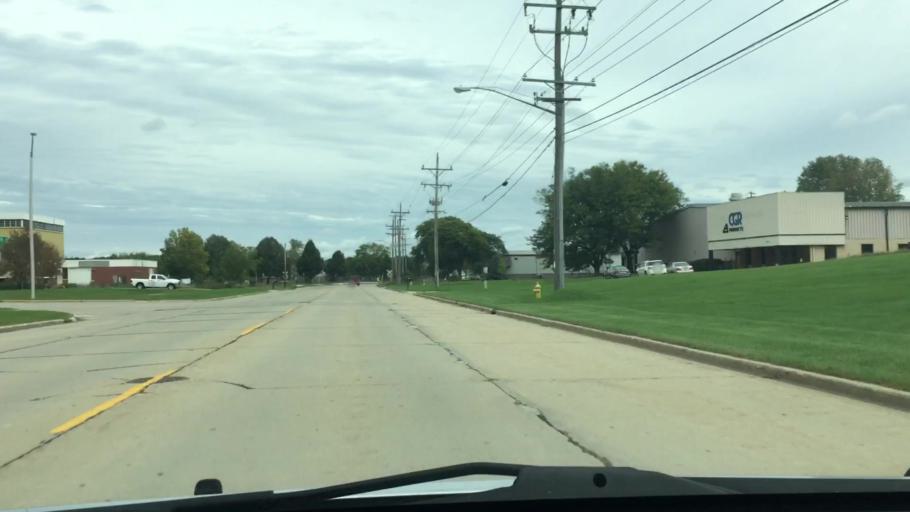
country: US
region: Wisconsin
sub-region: Waukesha County
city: Waukesha
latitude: 42.9921
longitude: -88.2497
